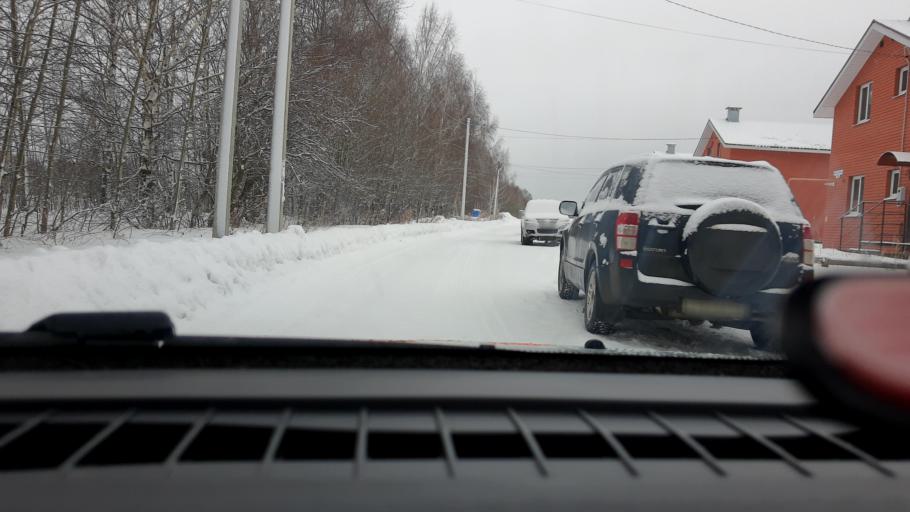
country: RU
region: Nizjnij Novgorod
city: Afonino
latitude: 56.2000
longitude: 44.0676
